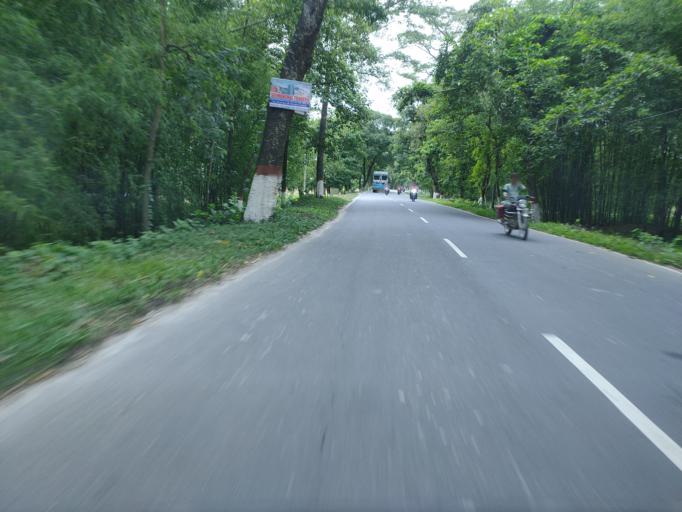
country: IN
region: West Bengal
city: Kishanganj
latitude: 26.1721
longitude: 87.9119
